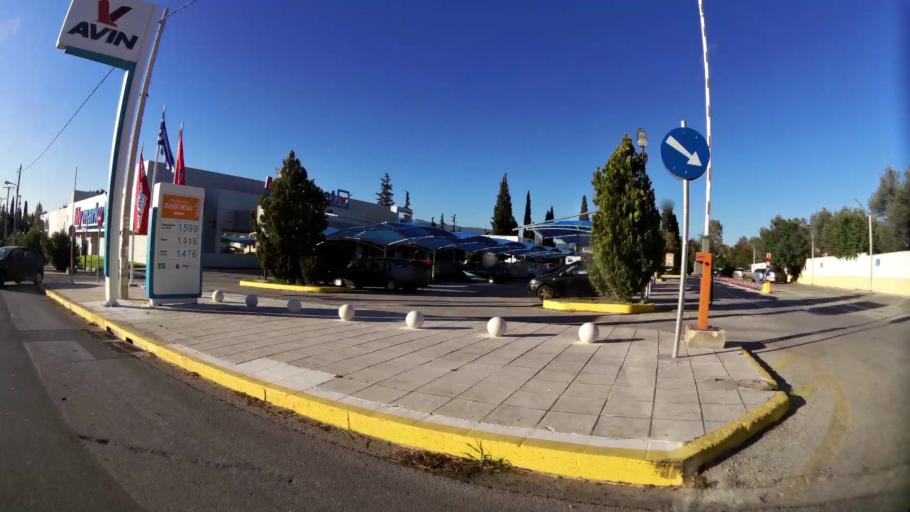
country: GR
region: Attica
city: Pefki
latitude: 38.0745
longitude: 23.7961
